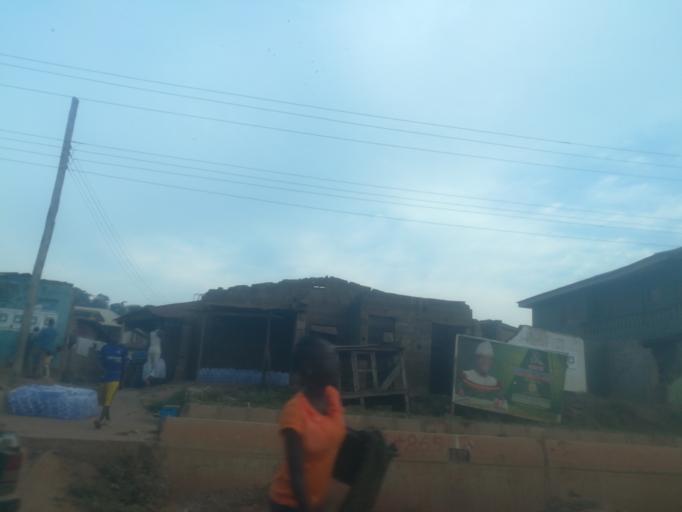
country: NG
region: Ogun
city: Abeokuta
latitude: 7.1702
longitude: 3.3380
